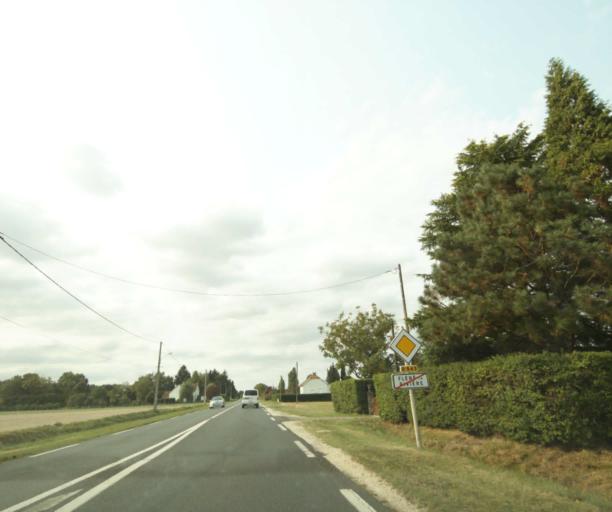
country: FR
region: Centre
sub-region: Departement de l'Indre
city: Chatillon-sur-Indre
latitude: 47.0234
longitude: 1.1045
